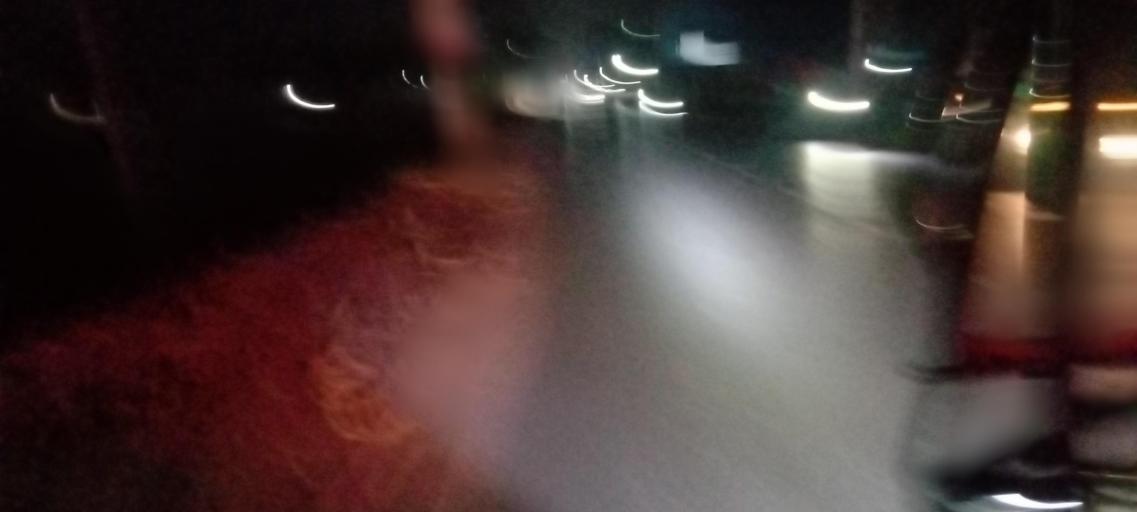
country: BD
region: Dhaka
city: Azimpur
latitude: 23.7002
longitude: 90.3720
